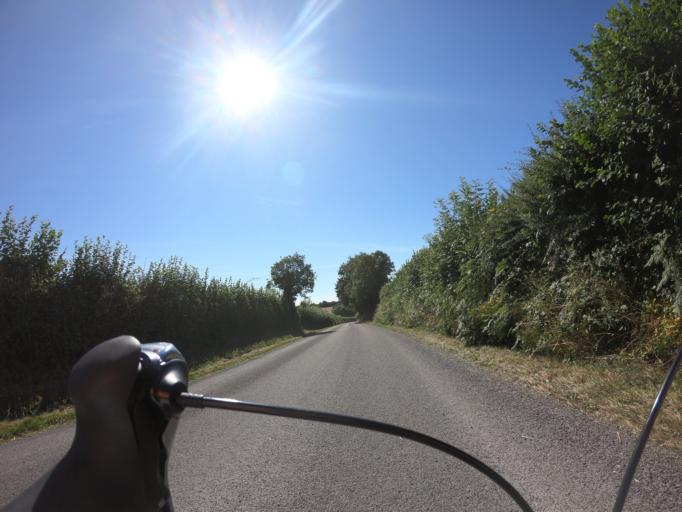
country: FR
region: Lower Normandy
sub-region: Departement de l'Orne
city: Saint-Denis-sur-Sarthon
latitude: 48.5432
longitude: -0.1038
